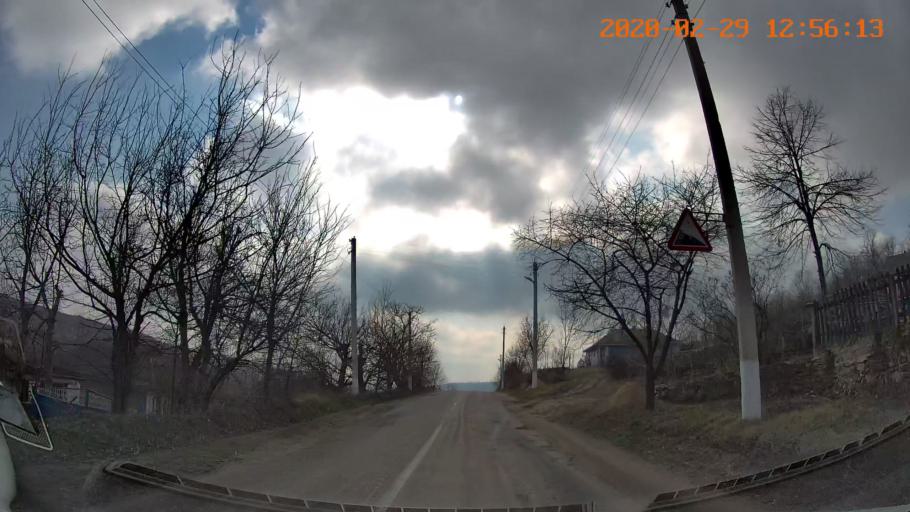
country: MD
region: Telenesti
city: Camenca
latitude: 48.0889
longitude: 28.7230
